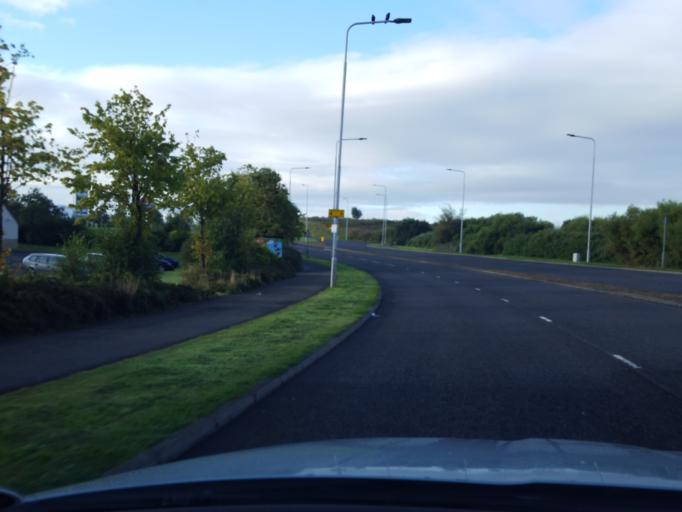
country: GB
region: Scotland
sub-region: Fife
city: Crossgates
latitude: 56.0793
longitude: -3.4000
